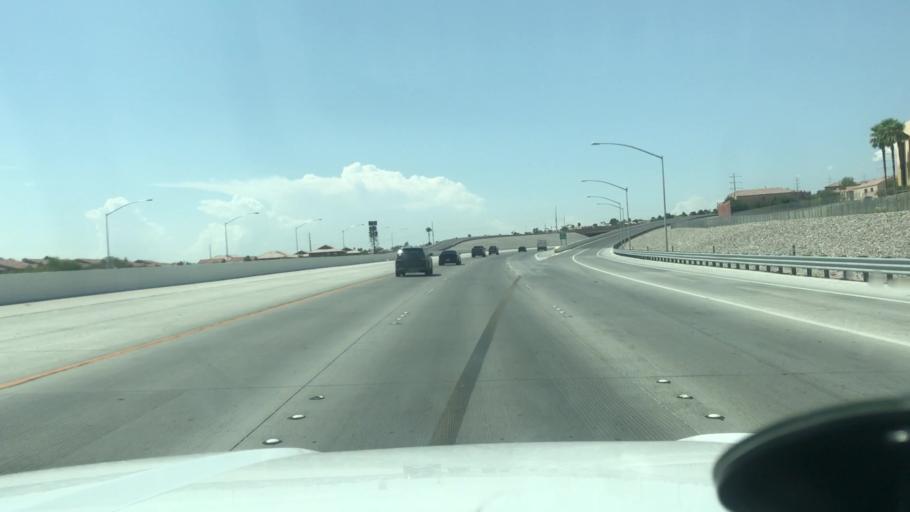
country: US
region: Nevada
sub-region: Clark County
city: Summerlin South
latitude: 36.2259
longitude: -115.3257
